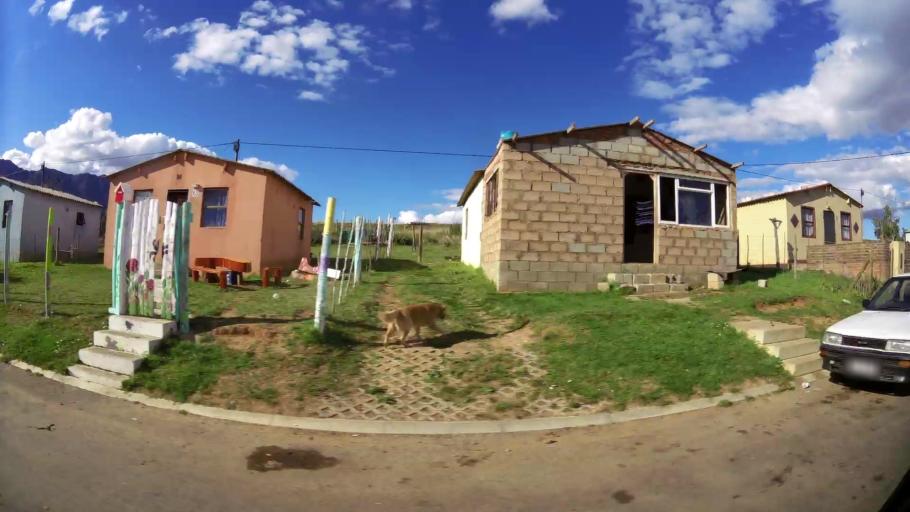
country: ZA
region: Western Cape
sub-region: Overberg District Municipality
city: Swellendam
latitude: -34.0328
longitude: 20.4517
